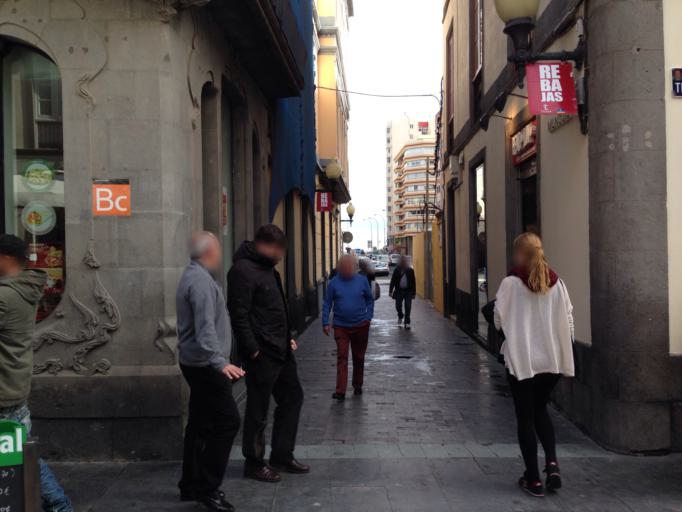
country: ES
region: Canary Islands
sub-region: Provincia de Las Palmas
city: Las Palmas de Gran Canaria
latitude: 28.1061
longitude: -15.4164
